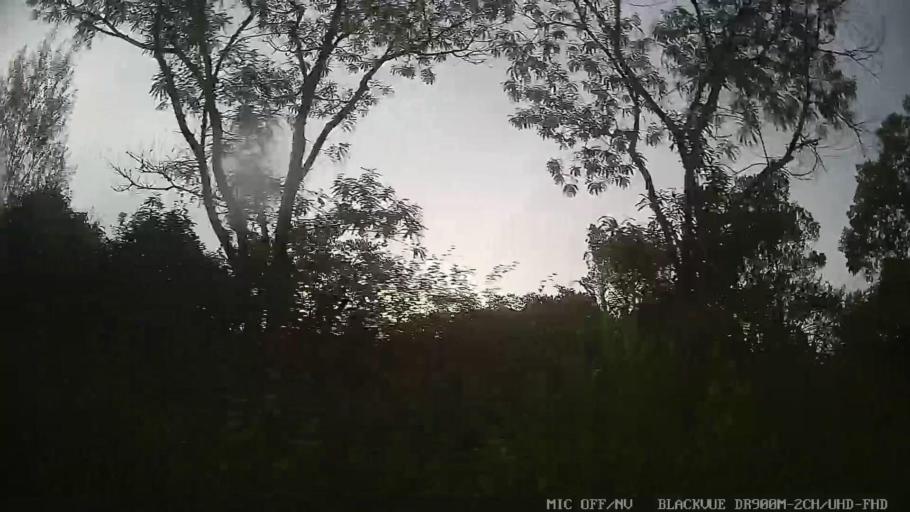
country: BR
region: Sao Paulo
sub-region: Ribeirao Pires
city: Ribeirao Pires
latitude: -23.6948
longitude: -46.3661
